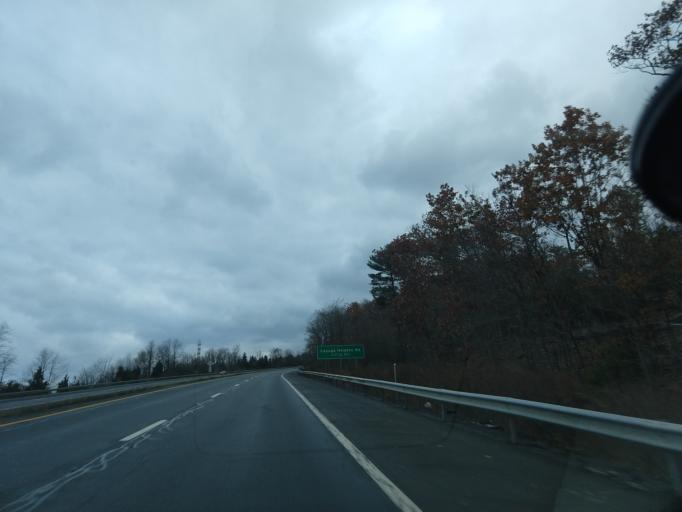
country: US
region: New York
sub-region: Tompkins County
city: Cayuga Heights
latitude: 42.4710
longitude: -76.5002
